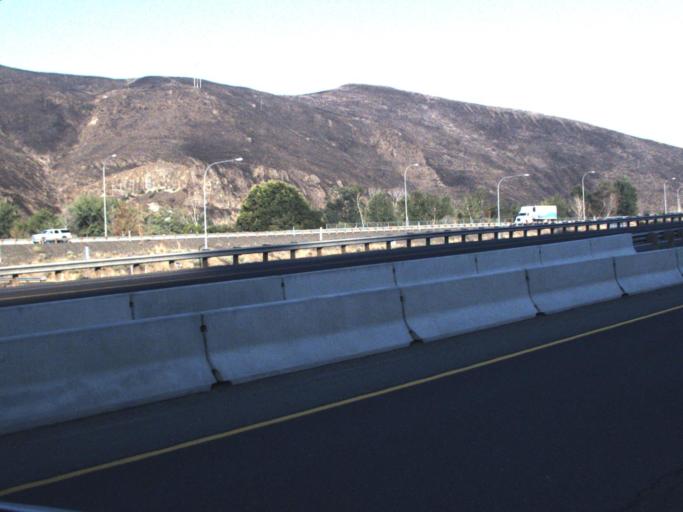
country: US
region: Washington
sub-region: Yakima County
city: Selah
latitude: 46.6339
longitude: -120.5206
